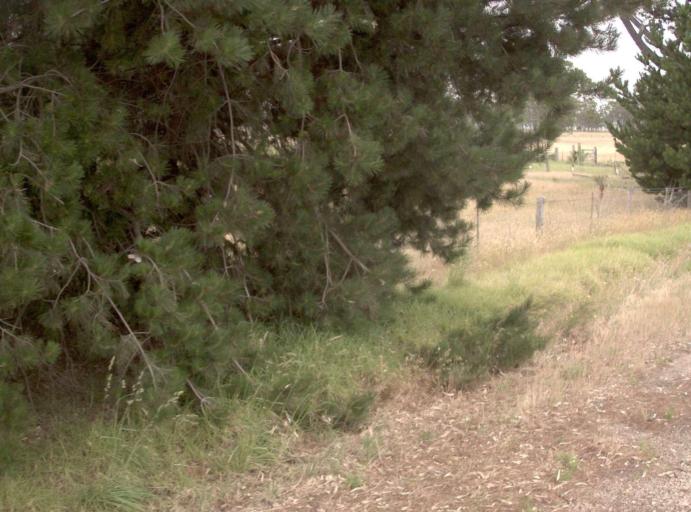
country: AU
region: Victoria
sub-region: East Gippsland
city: Bairnsdale
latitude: -37.8203
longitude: 147.4356
